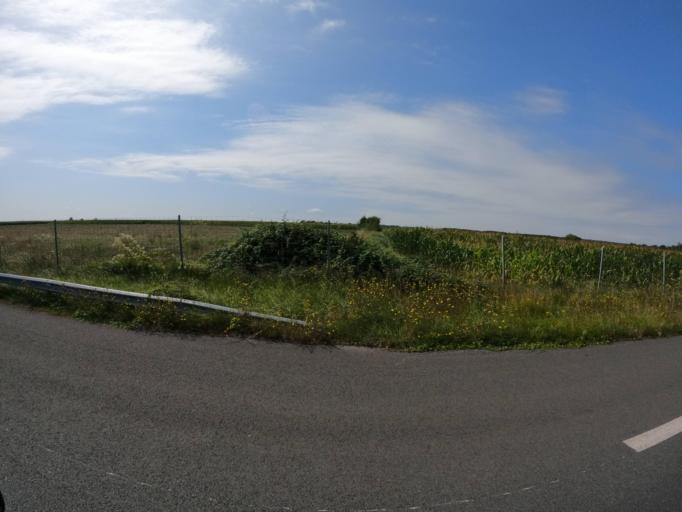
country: FR
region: Poitou-Charentes
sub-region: Departement des Deux-Sevres
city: Mauze-sur-le-Mignon
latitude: 46.1958
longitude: -0.6951
